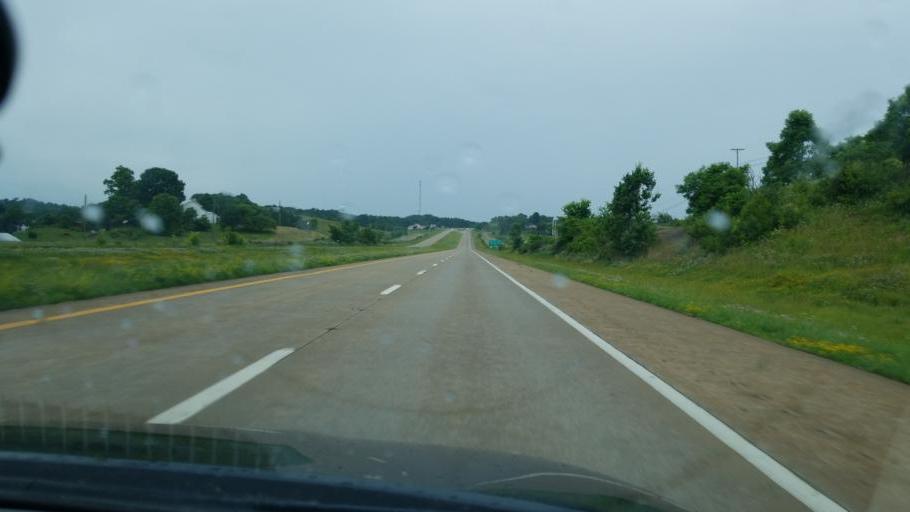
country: US
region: West Virginia
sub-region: Wood County
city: Washington
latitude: 39.2238
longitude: -81.8704
